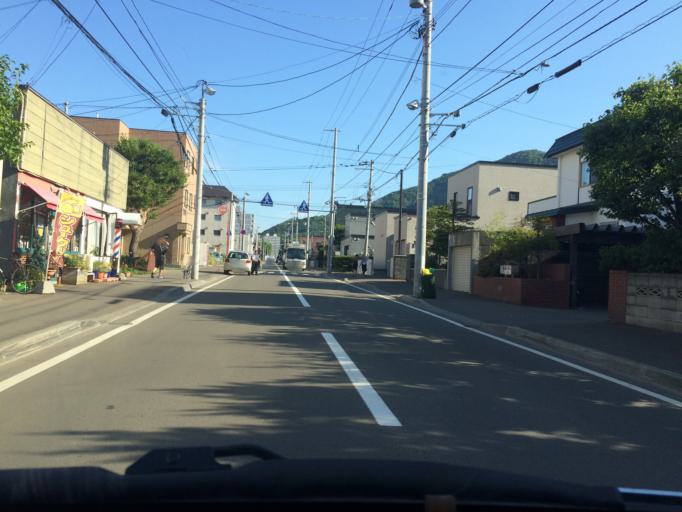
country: JP
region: Hokkaido
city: Sapporo
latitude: 43.0331
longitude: 141.3411
